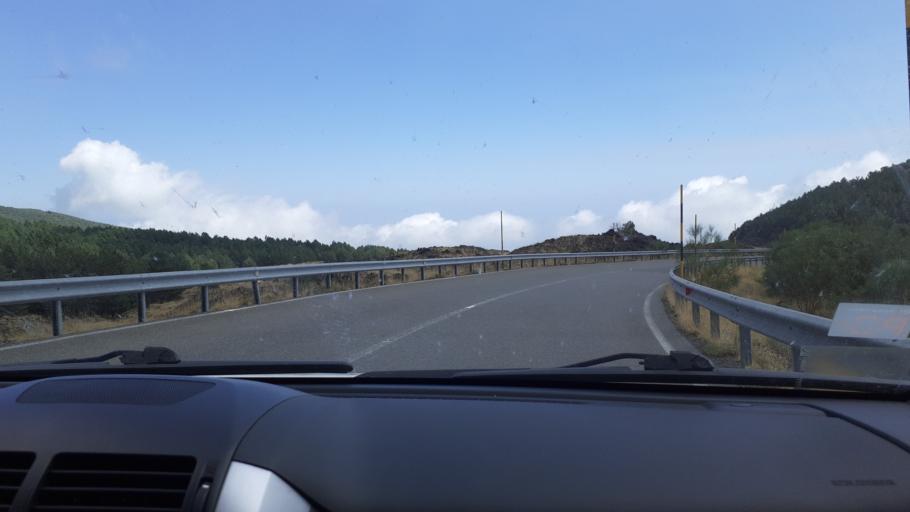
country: IT
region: Sicily
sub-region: Catania
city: Nicolosi
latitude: 37.6951
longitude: 15.0194
